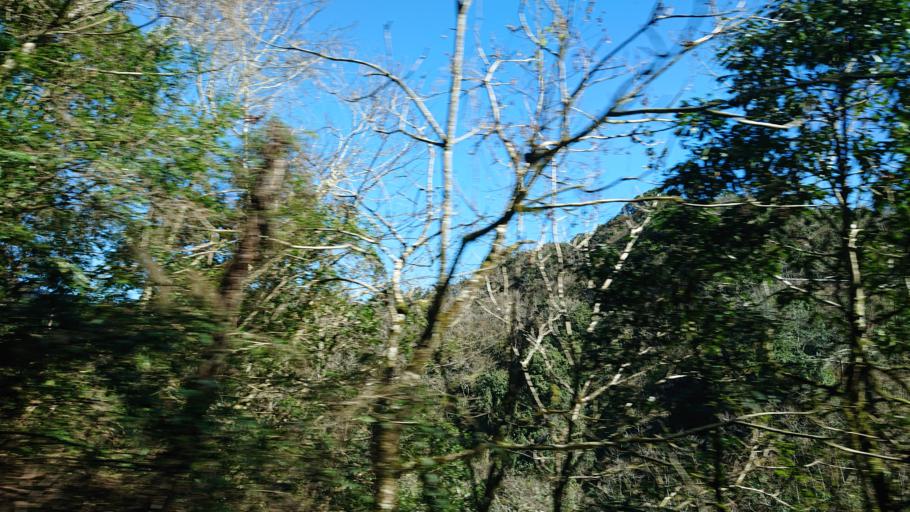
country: TW
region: Taiwan
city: Daxi
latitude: 24.4039
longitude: 121.3654
